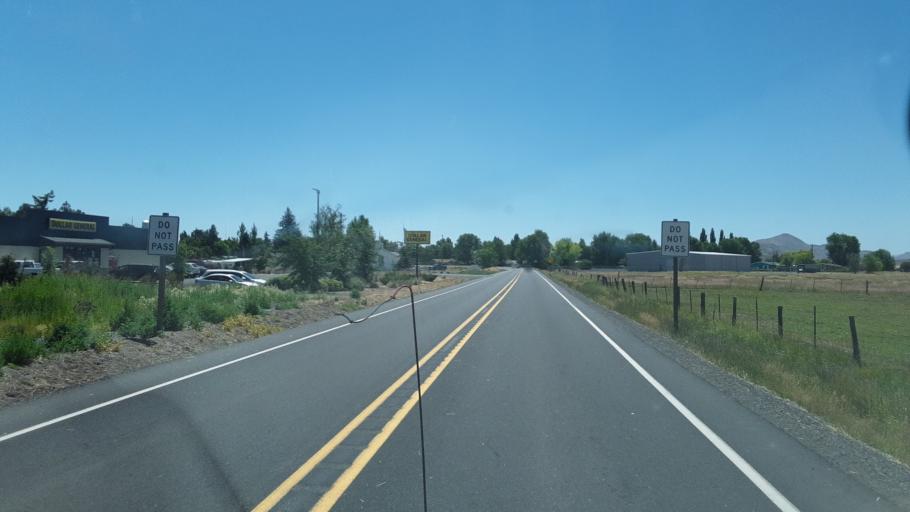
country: US
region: California
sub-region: Siskiyou County
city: Tulelake
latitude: 42.0266
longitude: -121.6101
